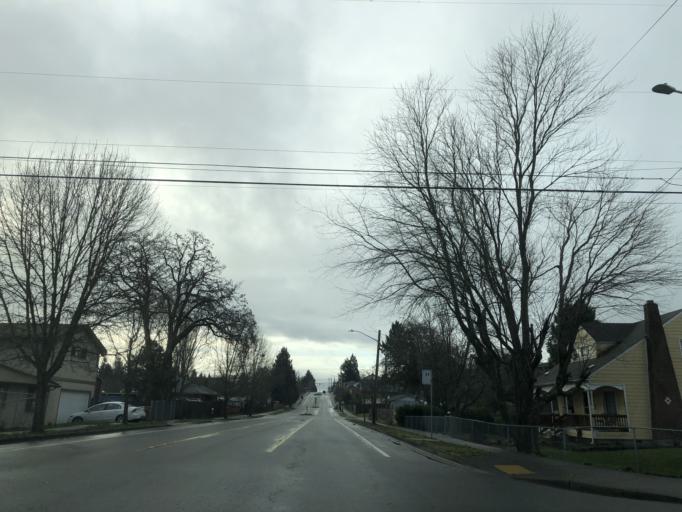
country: US
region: Washington
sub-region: Pierce County
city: Tacoma
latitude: 47.2167
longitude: -122.4583
